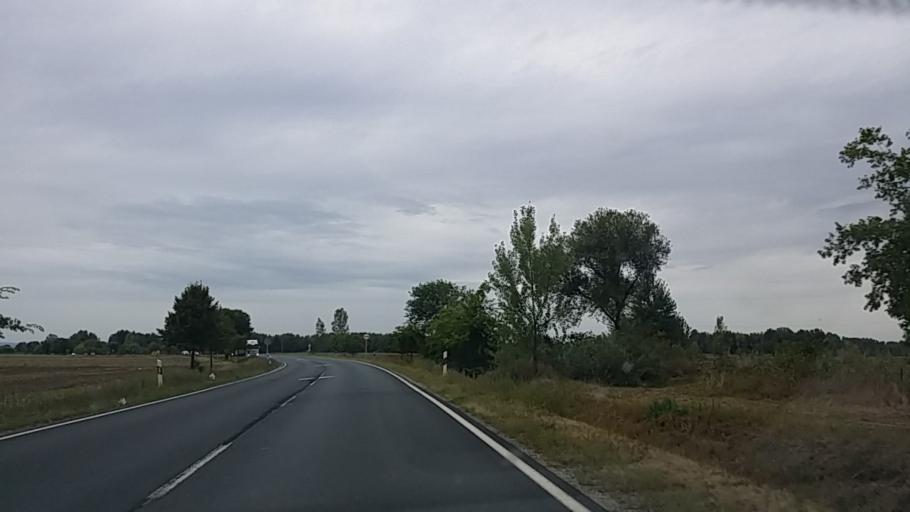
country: HU
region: Gyor-Moson-Sopron
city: Fertoszentmiklos
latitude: 47.5911
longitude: 16.8507
